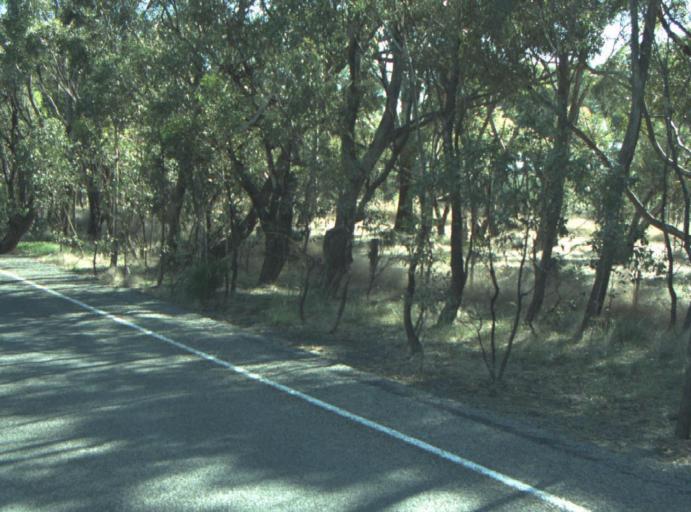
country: AU
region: Victoria
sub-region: Greater Geelong
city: Lara
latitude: -37.9184
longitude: 144.3969
